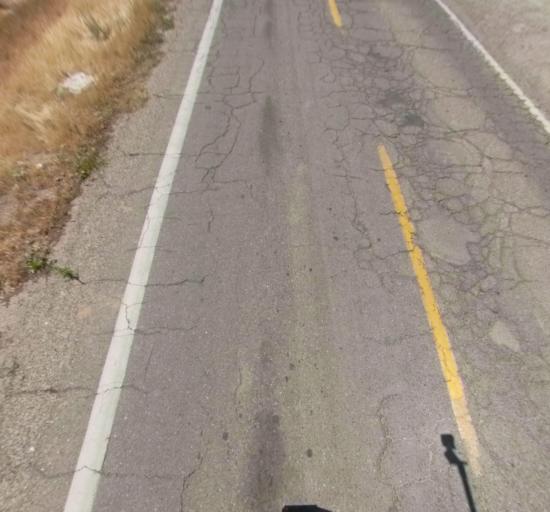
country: US
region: California
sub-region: Madera County
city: Fairmead
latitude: 37.0412
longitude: -120.2023
